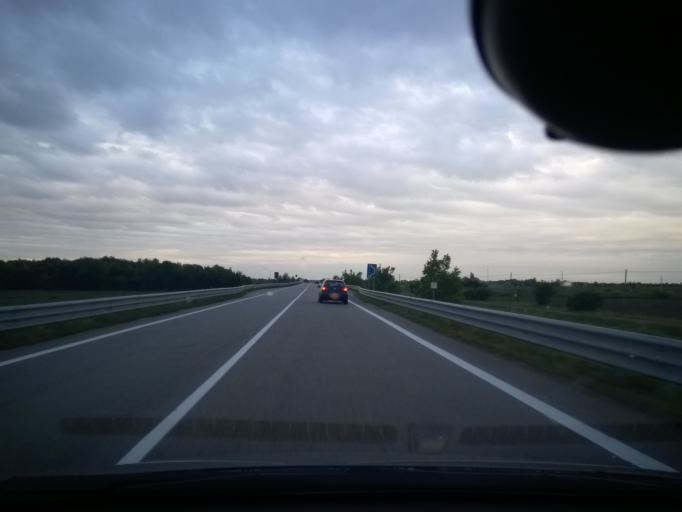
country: IT
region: Veneto
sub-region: Provincia di Venezia
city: Musile di Piave
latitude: 45.6071
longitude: 12.5098
